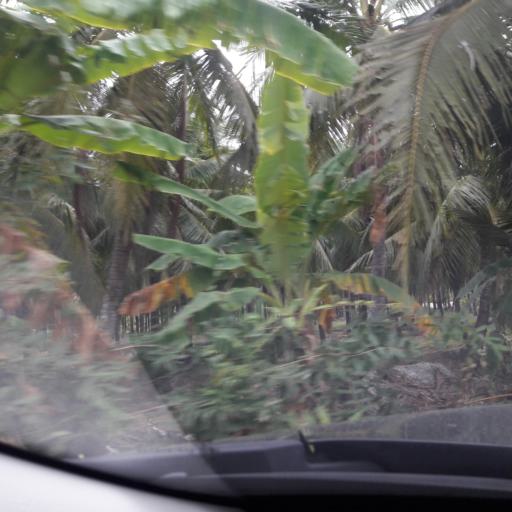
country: TH
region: Ratchaburi
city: Damnoen Saduak
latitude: 13.5730
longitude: 99.9452
